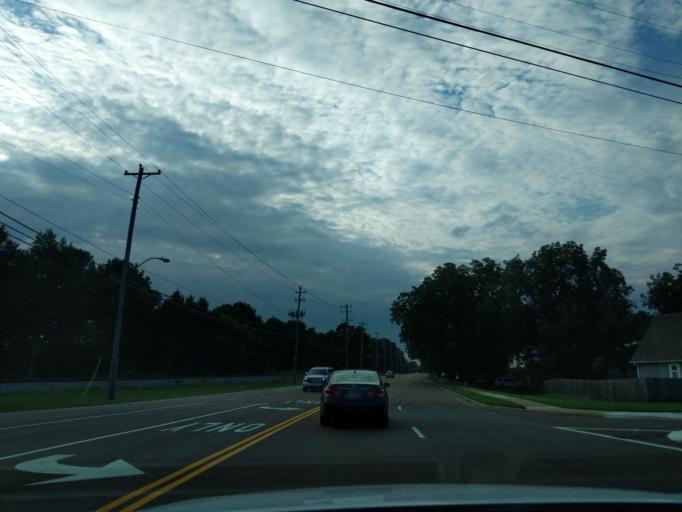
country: US
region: Tennessee
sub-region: Shelby County
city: Germantown
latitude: 35.0746
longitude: -89.7944
